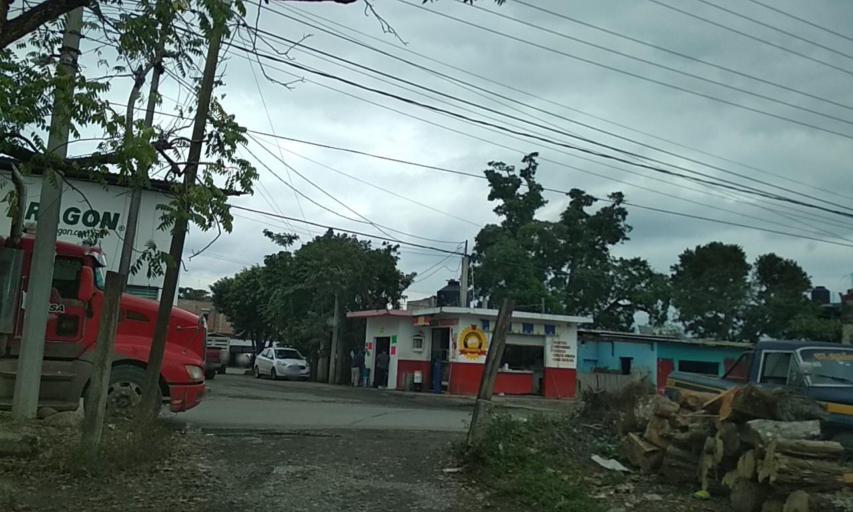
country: MX
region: Veracruz
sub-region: Papantla
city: El Chote
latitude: 20.3992
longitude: -97.3362
